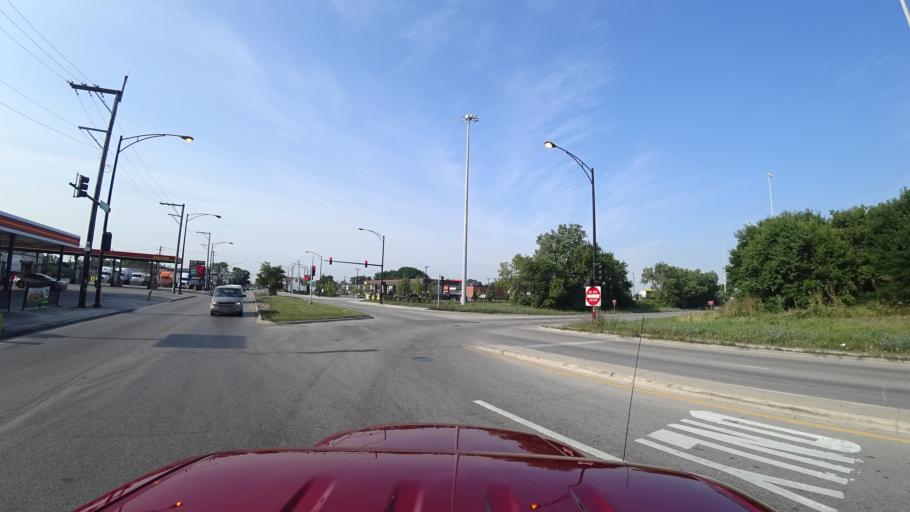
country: US
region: Illinois
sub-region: Cook County
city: Chicago
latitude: 41.8317
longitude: -87.6948
